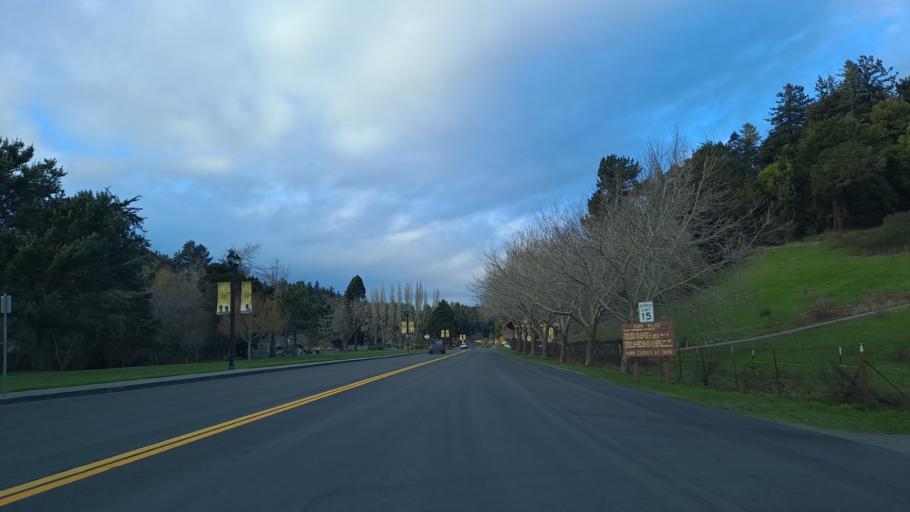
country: US
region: California
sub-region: Humboldt County
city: Fortuna
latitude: 40.5983
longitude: -124.1497
